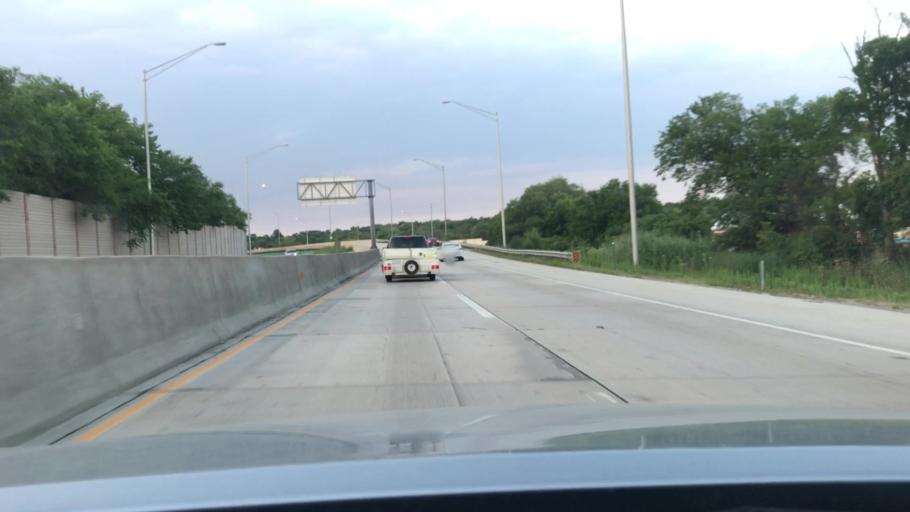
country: US
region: Illinois
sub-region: Cook County
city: Indian Head Park
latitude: 41.7681
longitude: -87.9079
